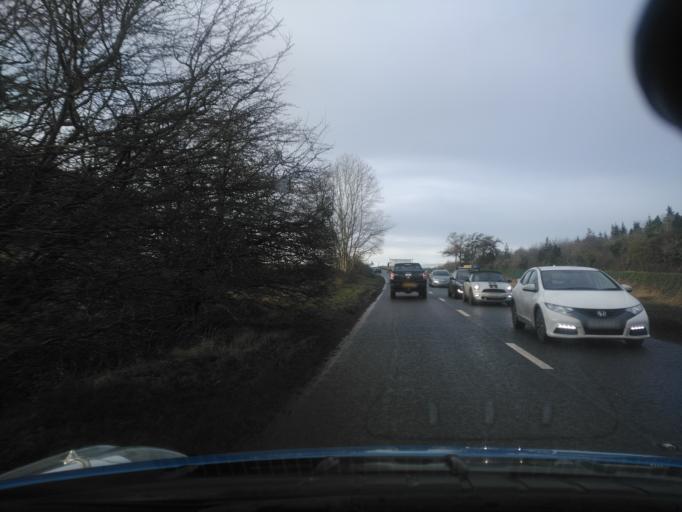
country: GB
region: England
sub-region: Gloucestershire
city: Chipping Campden
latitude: 51.9933
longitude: -1.7662
